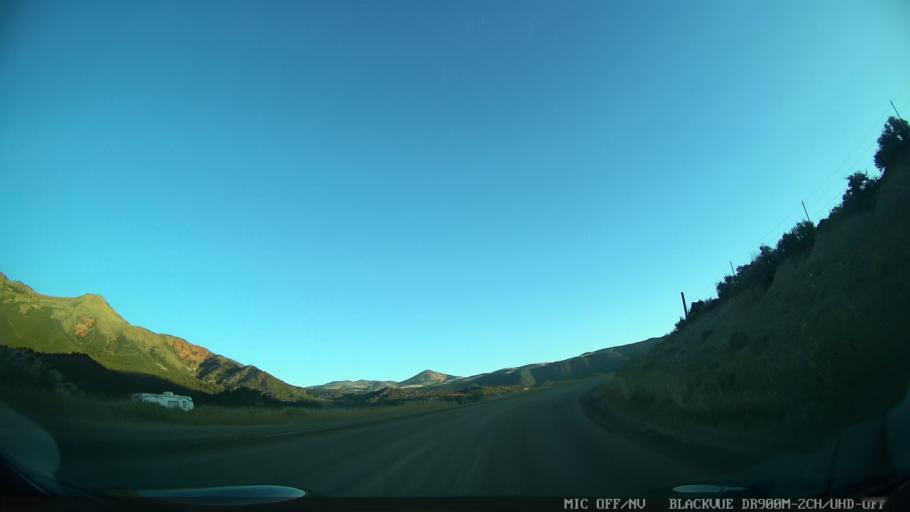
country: US
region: Colorado
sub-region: Eagle County
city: Edwards
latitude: 39.8980
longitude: -106.6067
